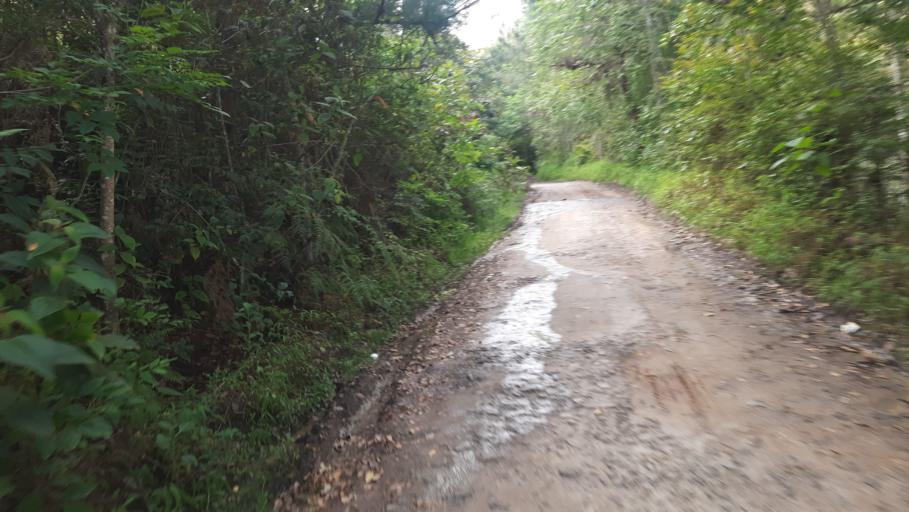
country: CO
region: Cundinamarca
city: Tenza
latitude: 5.1029
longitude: -73.4249
